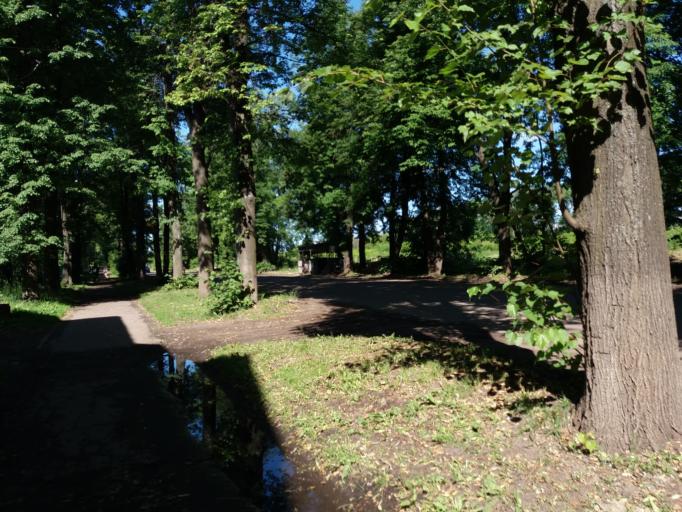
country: RU
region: Jaroslavl
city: Yaroslavl
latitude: 57.6426
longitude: 39.8333
